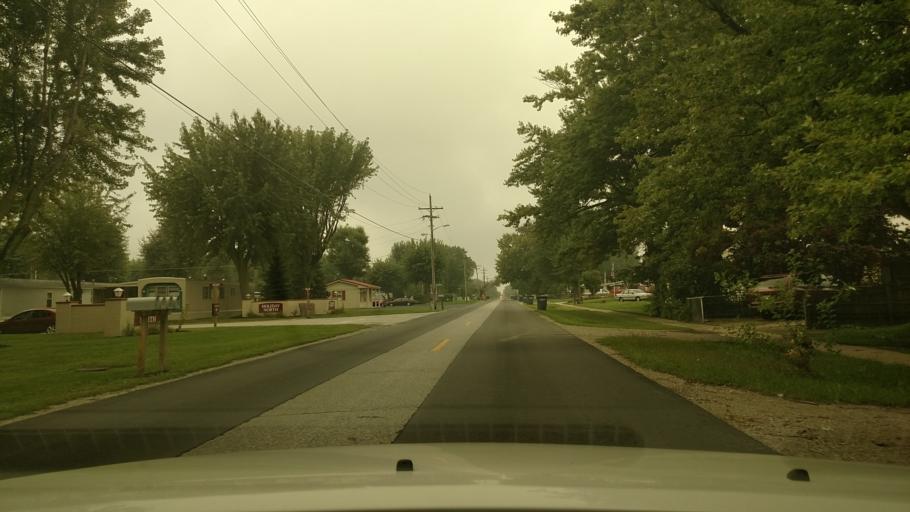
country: US
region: Indiana
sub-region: Howard County
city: Kokomo
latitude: 40.5171
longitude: -86.1270
